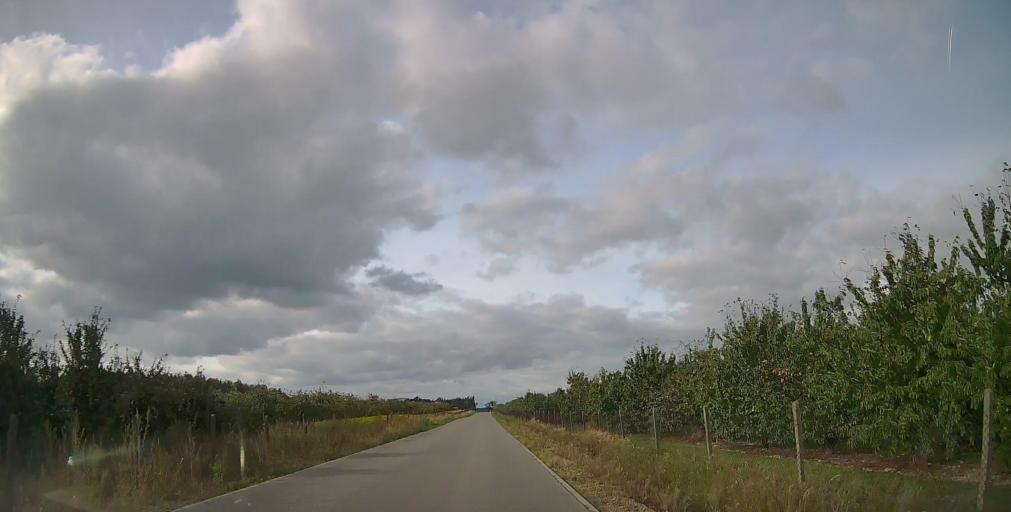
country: PL
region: Masovian Voivodeship
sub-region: Powiat bialobrzeski
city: Promna
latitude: 51.7486
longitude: 20.9632
